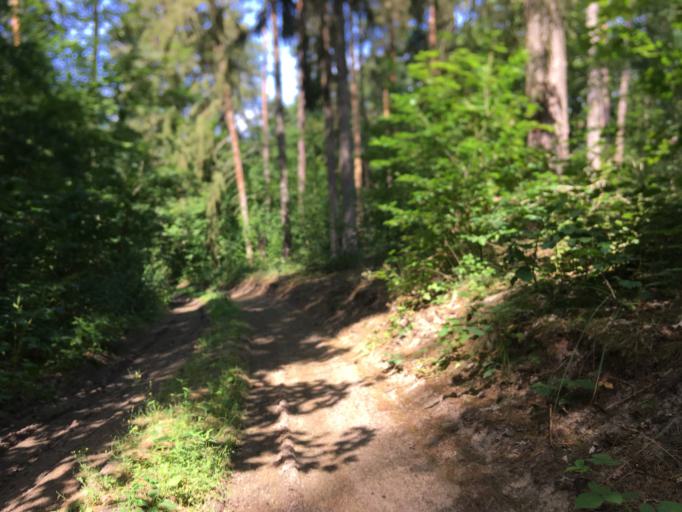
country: DE
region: Brandenburg
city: Casekow
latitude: 53.2304
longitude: 14.1313
